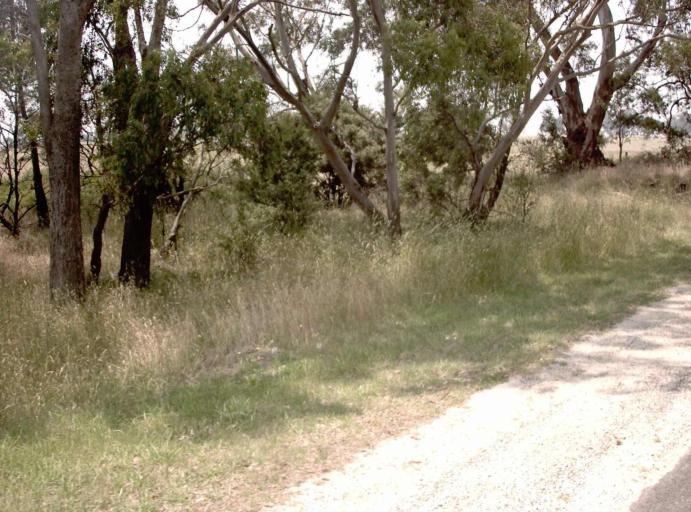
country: AU
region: Victoria
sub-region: Latrobe
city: Traralgon
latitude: -38.2471
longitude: 146.6504
